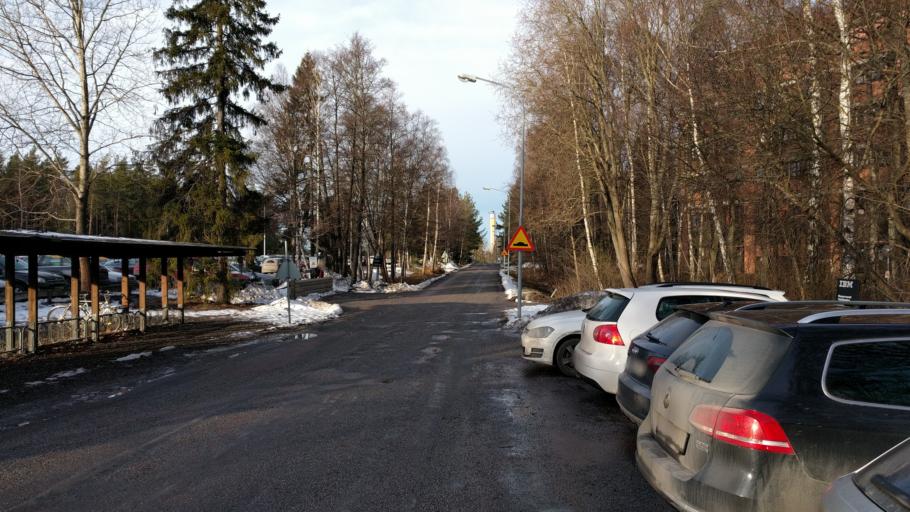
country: SE
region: Stockholm
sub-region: Stockholms Kommun
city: Kista
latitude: 59.4104
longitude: 17.9377
